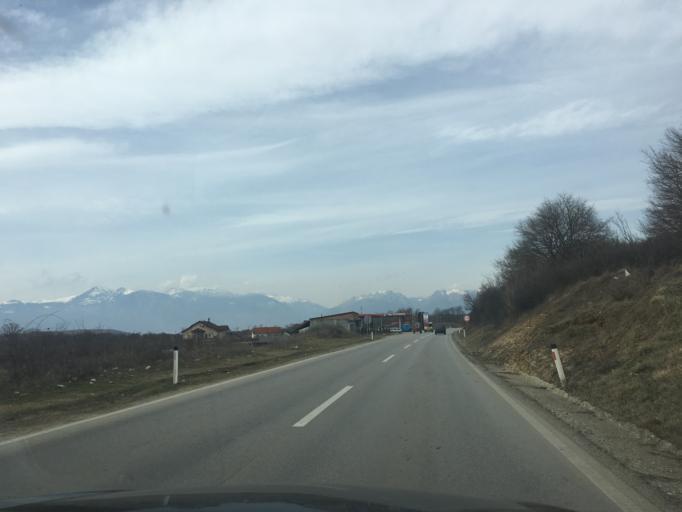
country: XK
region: Pec
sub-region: Komuna e Pejes
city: Kosuriq
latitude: 42.6173
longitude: 20.4920
